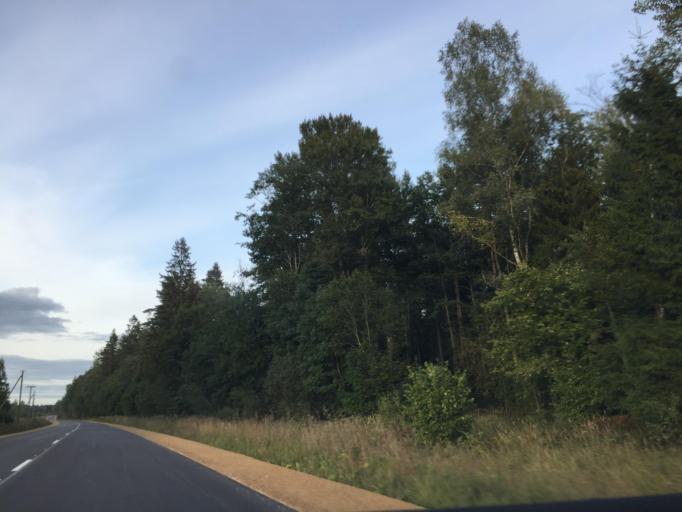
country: LV
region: Viesite
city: Viesite
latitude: 56.3806
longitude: 25.6662
